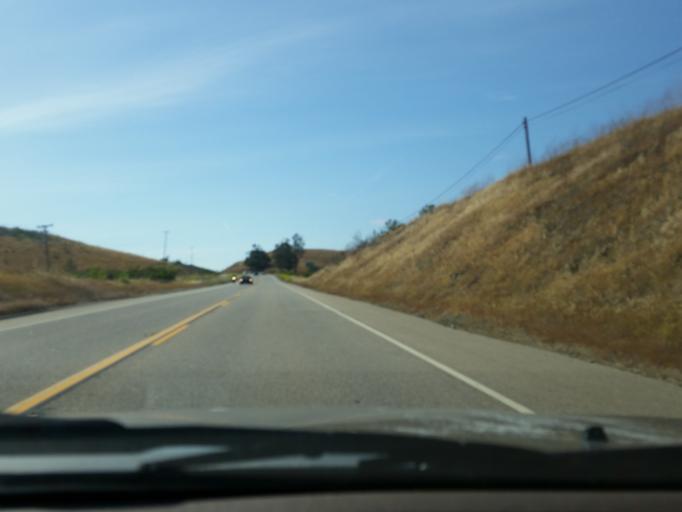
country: US
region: California
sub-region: San Luis Obispo County
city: Cambria
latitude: 35.4999
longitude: -121.0116
